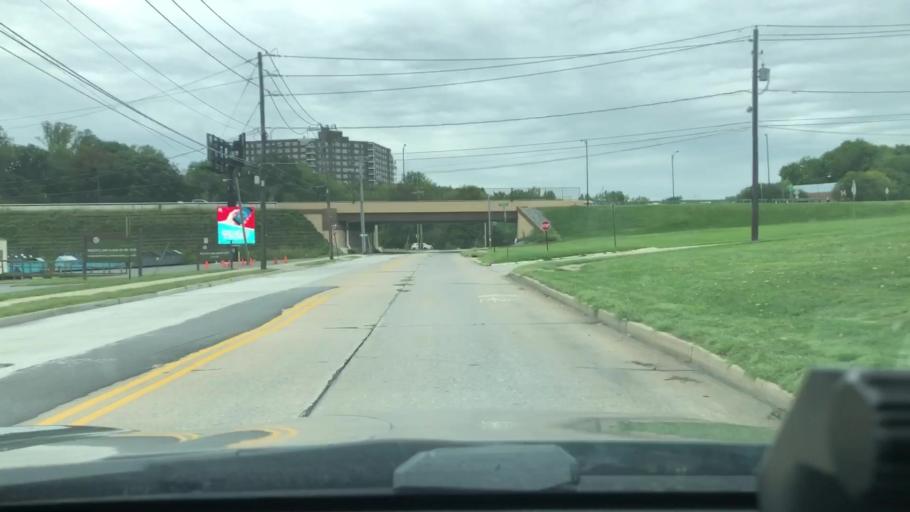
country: US
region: Pennsylvania
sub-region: Lehigh County
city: Allentown
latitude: 40.5925
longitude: -75.4831
